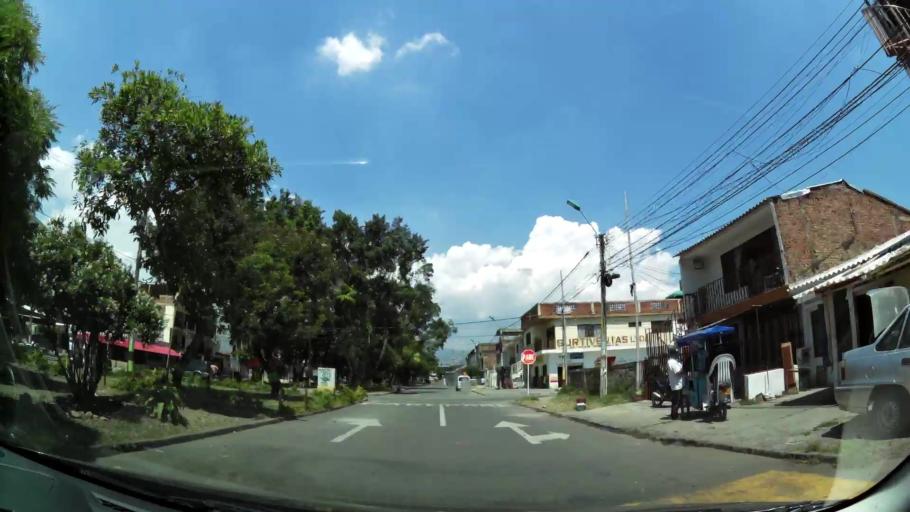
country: CO
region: Valle del Cauca
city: Cali
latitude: 3.4355
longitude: -76.4985
